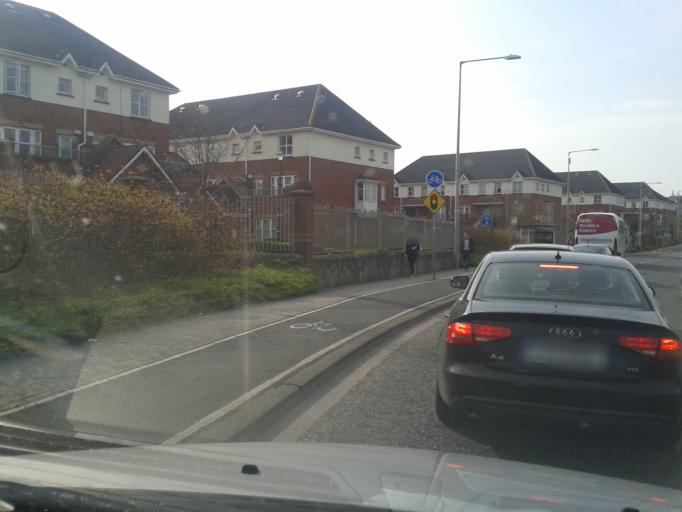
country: IE
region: Leinster
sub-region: Fingal County
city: Swords
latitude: 53.4448
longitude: -6.2343
